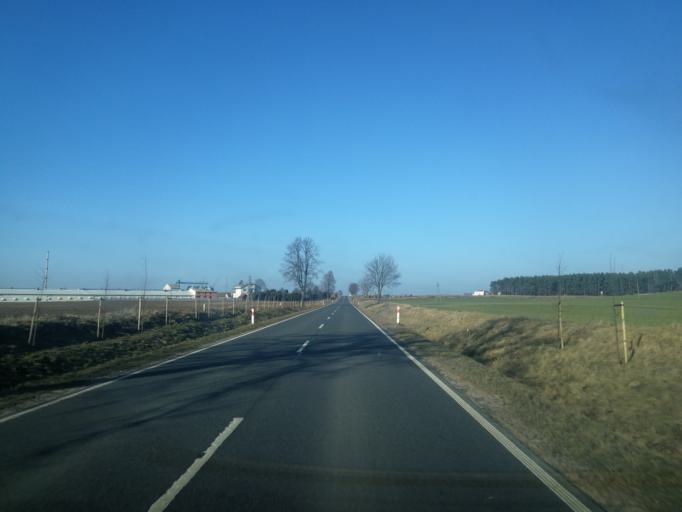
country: PL
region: Warmian-Masurian Voivodeship
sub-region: Powiat ilawski
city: Lubawa
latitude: 53.4326
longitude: 19.7745
